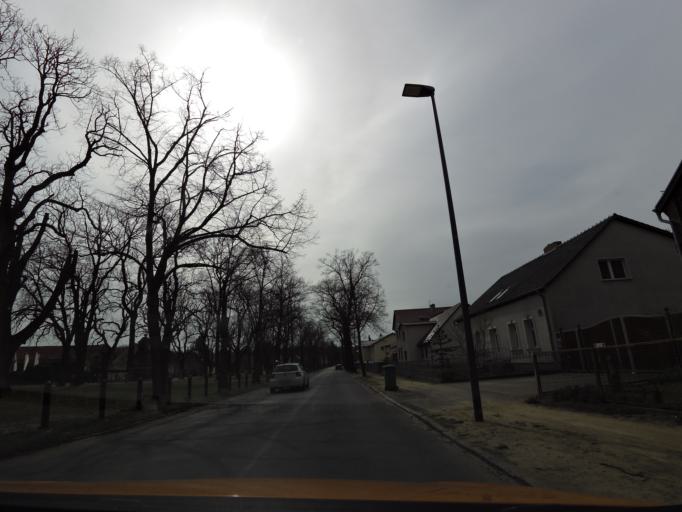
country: DE
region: Brandenburg
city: Rangsdorf
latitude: 52.3308
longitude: 13.3937
